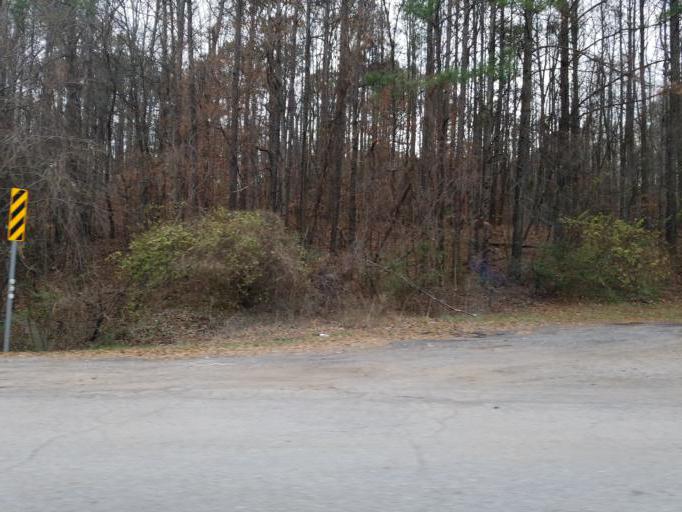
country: US
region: Georgia
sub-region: Cherokee County
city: Canton
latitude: 34.2215
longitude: -84.4980
